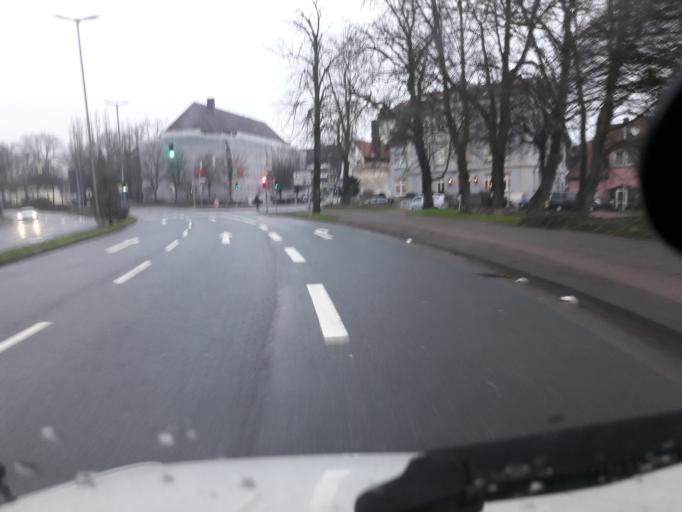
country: DE
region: North Rhine-Westphalia
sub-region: Regierungsbezirk Detmold
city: Minden
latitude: 52.2909
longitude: 8.9226
